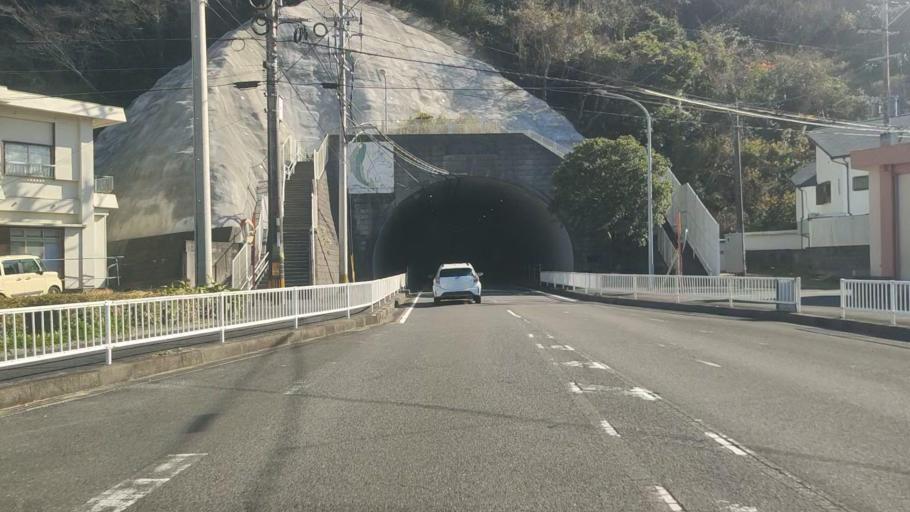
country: JP
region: Oita
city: Saiki
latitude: 32.8012
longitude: 131.9260
